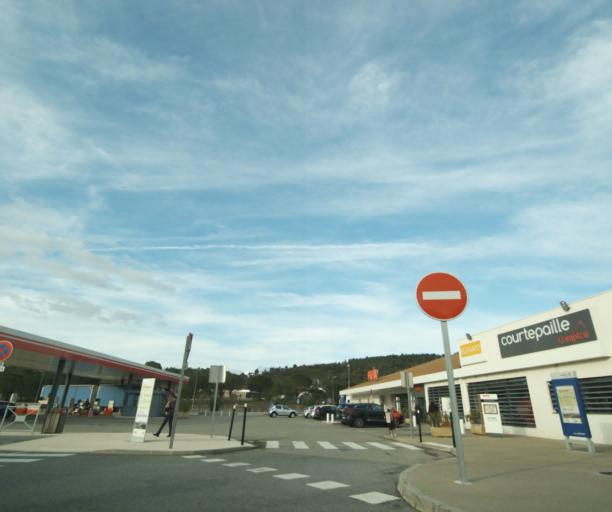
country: FR
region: Provence-Alpes-Cote d'Azur
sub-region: Departement du Var
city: Vidauban
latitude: 43.4140
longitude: 6.4532
